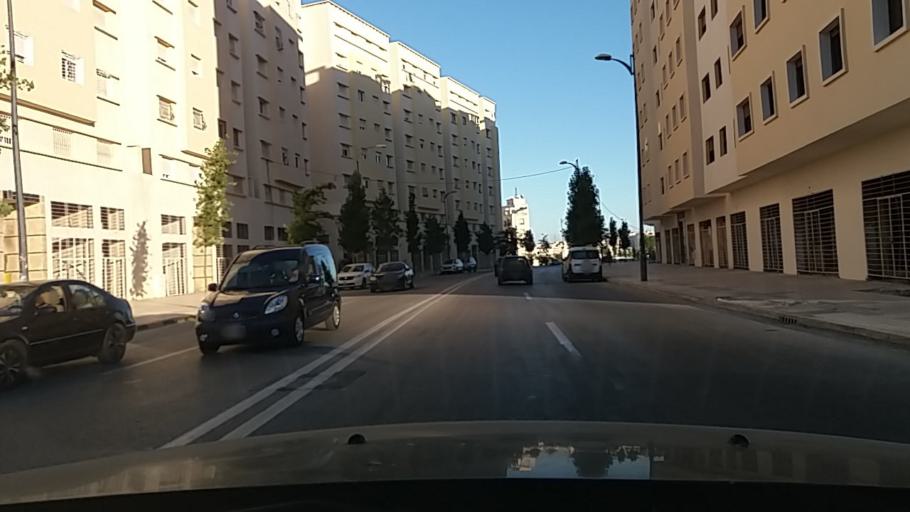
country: MA
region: Tanger-Tetouan
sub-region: Tanger-Assilah
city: Boukhalef
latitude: 35.7668
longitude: -5.8581
